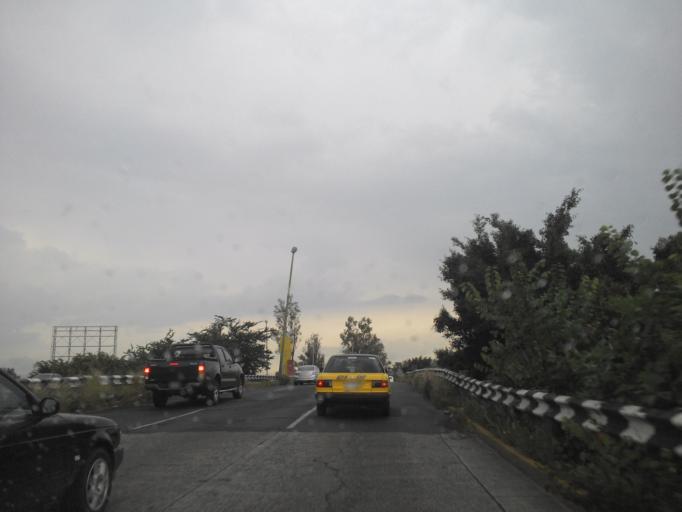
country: MX
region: Jalisco
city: Tlaquepaque
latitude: 20.6298
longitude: -103.3346
